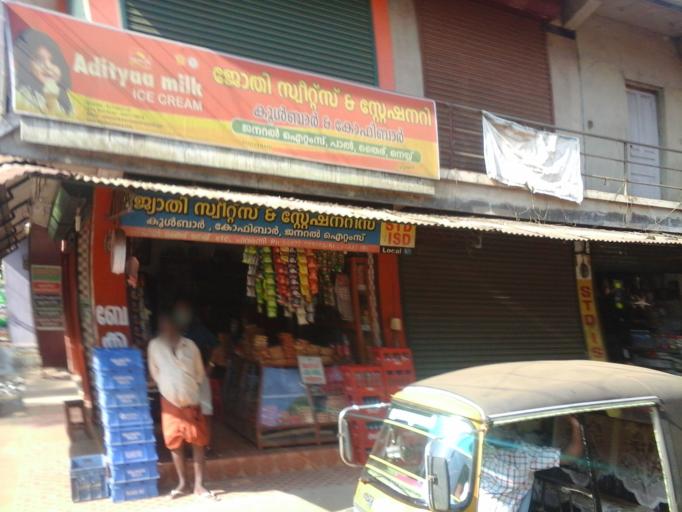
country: IN
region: Kerala
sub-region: Kottayam
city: Lalam
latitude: 9.6700
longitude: 76.7049
